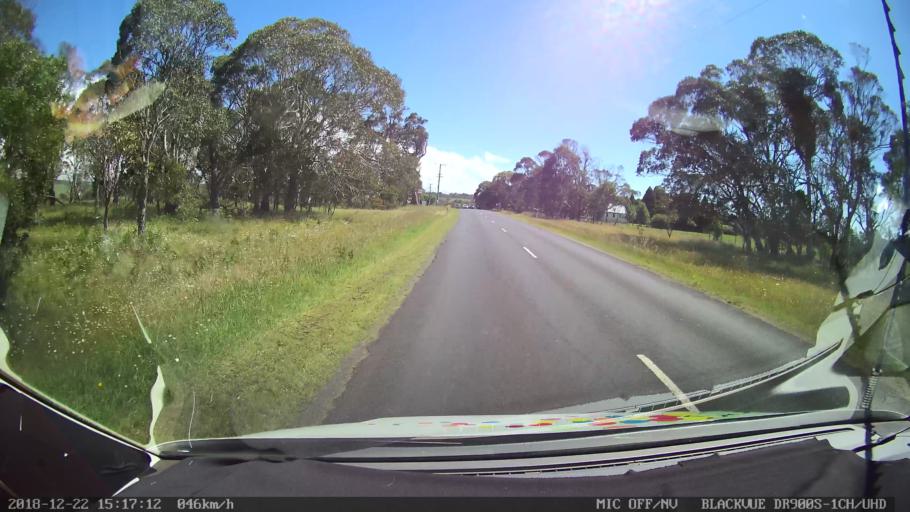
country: AU
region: New South Wales
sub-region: Bellingen
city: Dorrigo
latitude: -30.3965
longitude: 152.3536
